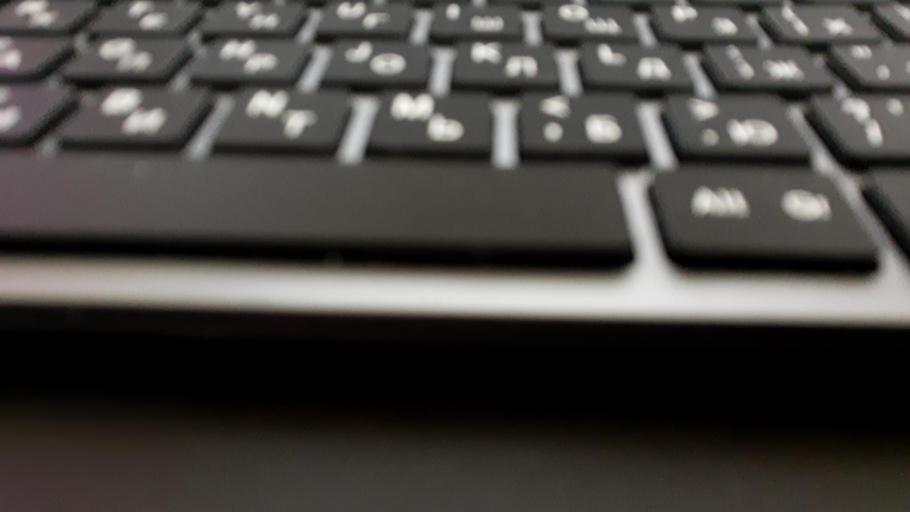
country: RU
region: Moskovskaya
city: Dorogomilovo
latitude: 55.7729
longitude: 37.5715
